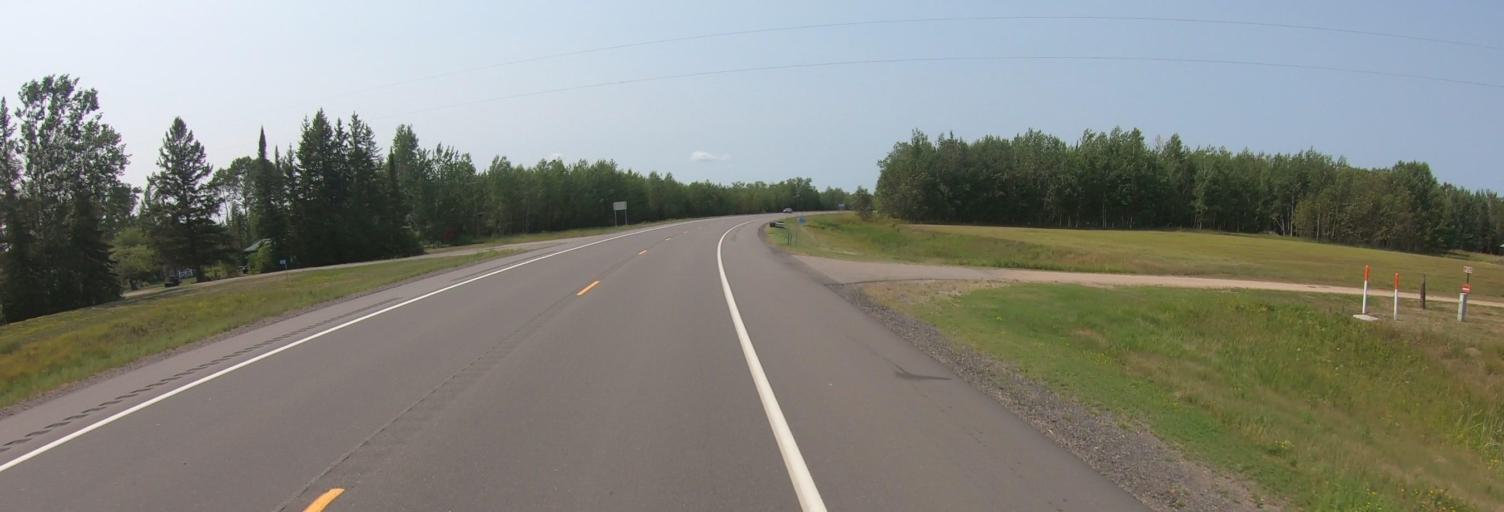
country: US
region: Minnesota
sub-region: Koochiching County
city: International Falls
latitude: 48.5238
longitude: -93.5341
